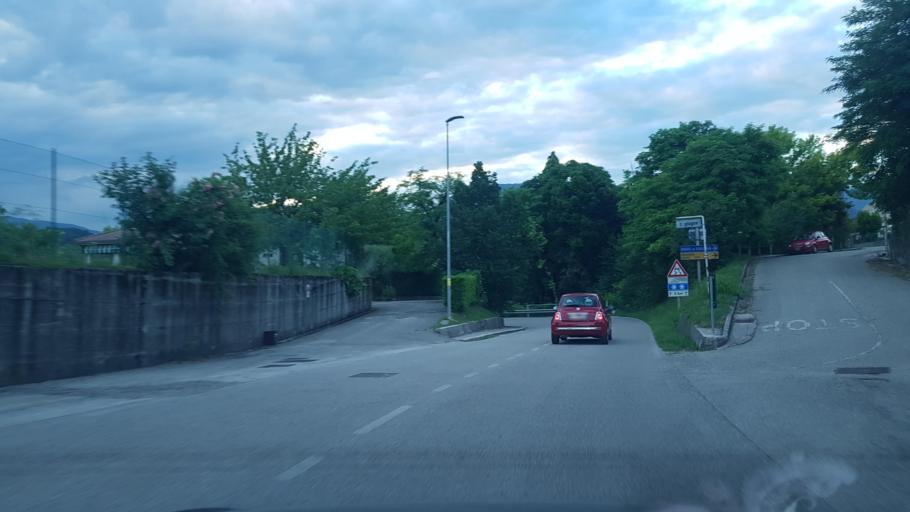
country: IT
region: Friuli Venezia Giulia
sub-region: Provincia di Pordenone
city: Pinzano al Tagliamento
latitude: 46.1823
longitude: 12.9603
